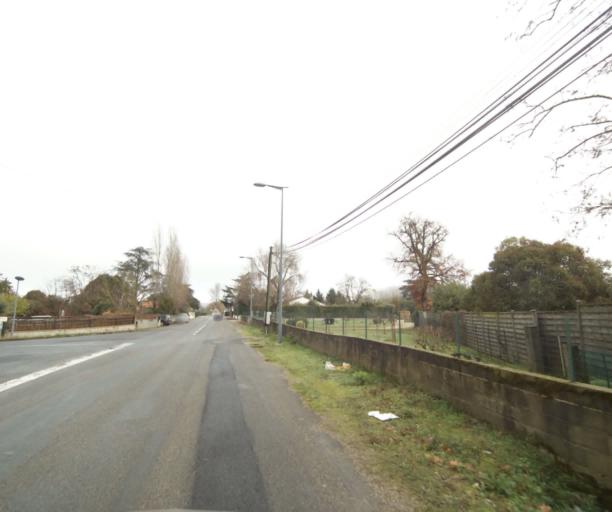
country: FR
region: Midi-Pyrenees
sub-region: Departement de la Haute-Garonne
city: Villemur-sur-Tarn
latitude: 43.8584
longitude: 1.4810
